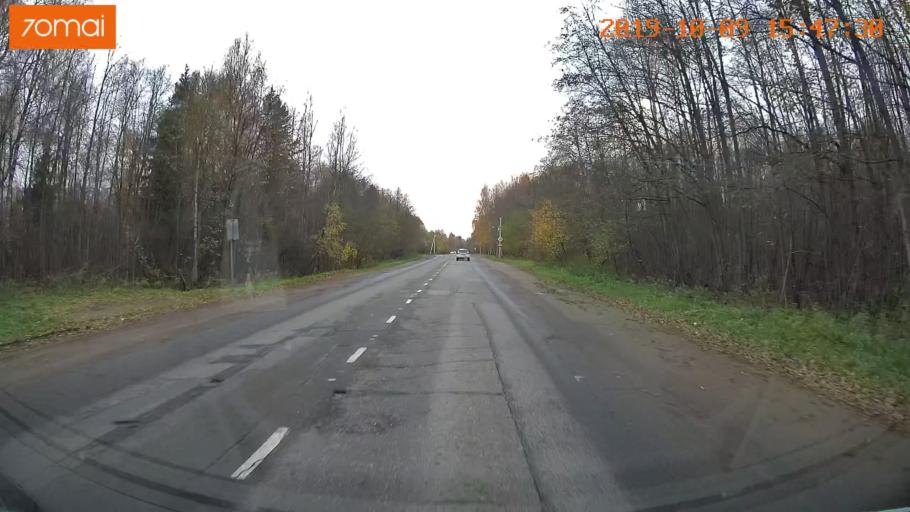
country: RU
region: Kostroma
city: Oktyabr'skiy
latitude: 57.8171
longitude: 41.0278
